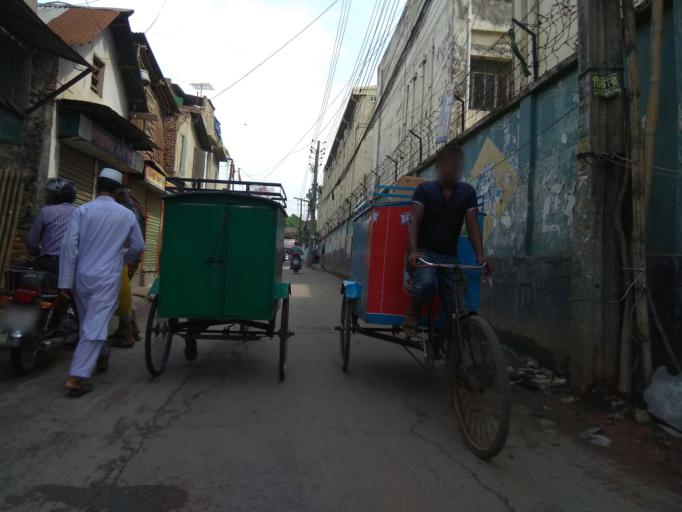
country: BD
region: Dhaka
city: Azimpur
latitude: 23.8002
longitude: 90.3584
